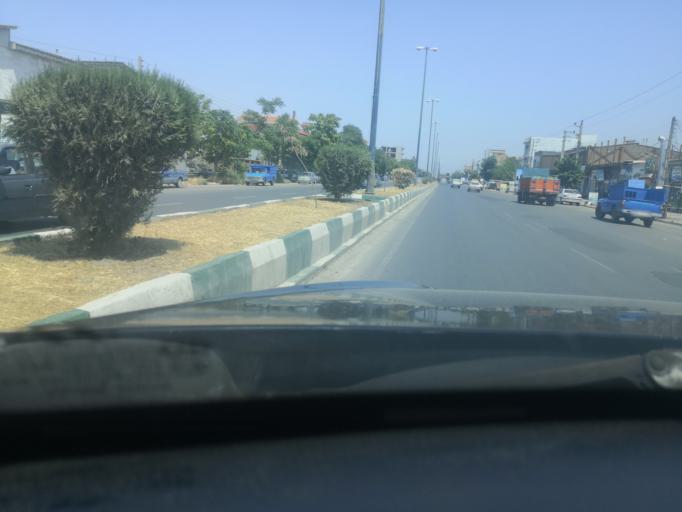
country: IR
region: Golestan
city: Aq Qala
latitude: 37.0091
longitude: 54.4651
